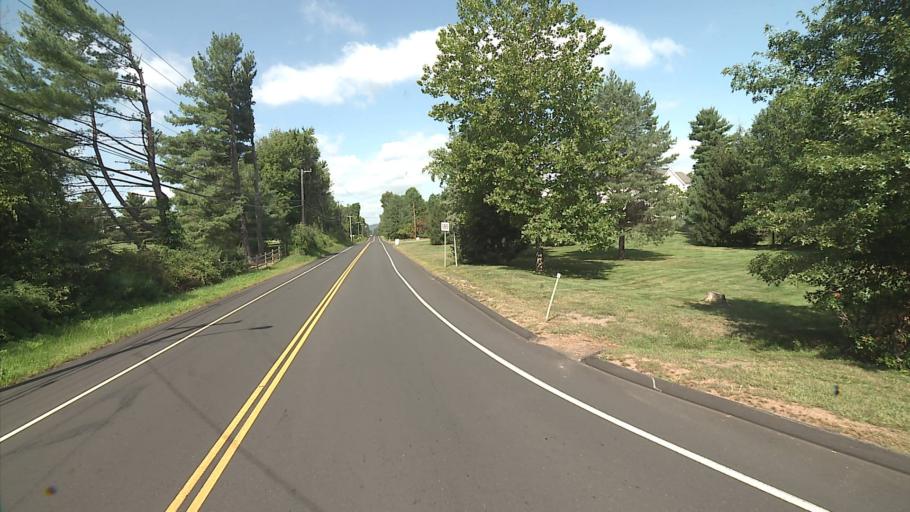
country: US
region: Connecticut
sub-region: Hartford County
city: Blue Hills
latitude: 41.7972
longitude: -72.7222
